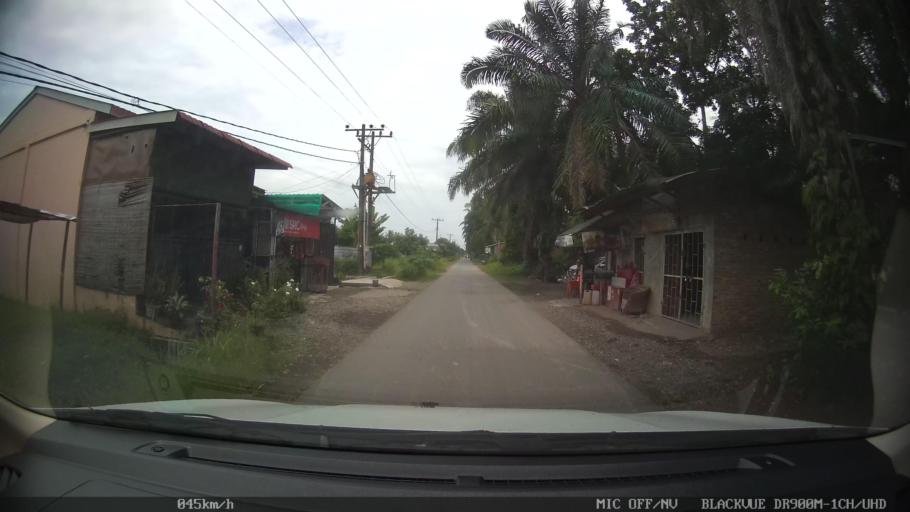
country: ID
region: North Sumatra
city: Sunggal
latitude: 3.6332
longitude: 98.5682
